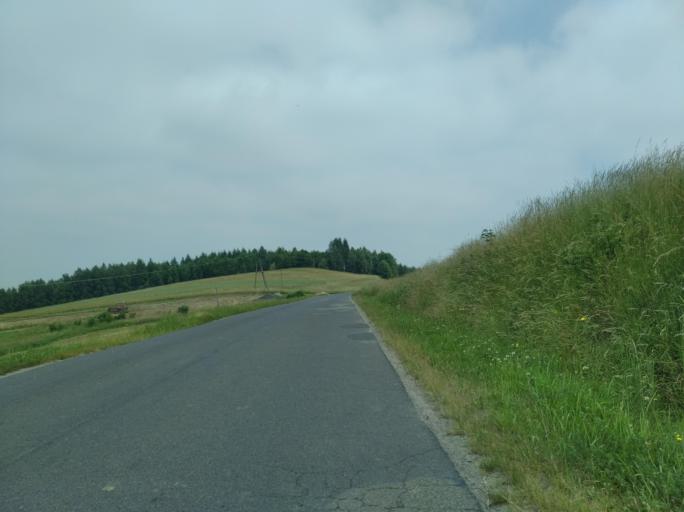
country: PL
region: Subcarpathian Voivodeship
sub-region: Powiat sanocki
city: Besko
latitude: 49.5765
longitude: 21.9475
